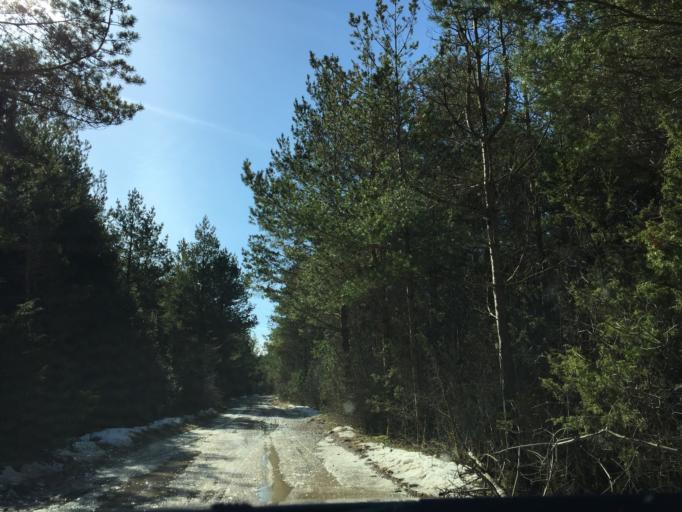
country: EE
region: Laeaene
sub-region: Haapsalu linn
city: Haapsalu
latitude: 58.6409
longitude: 23.5174
